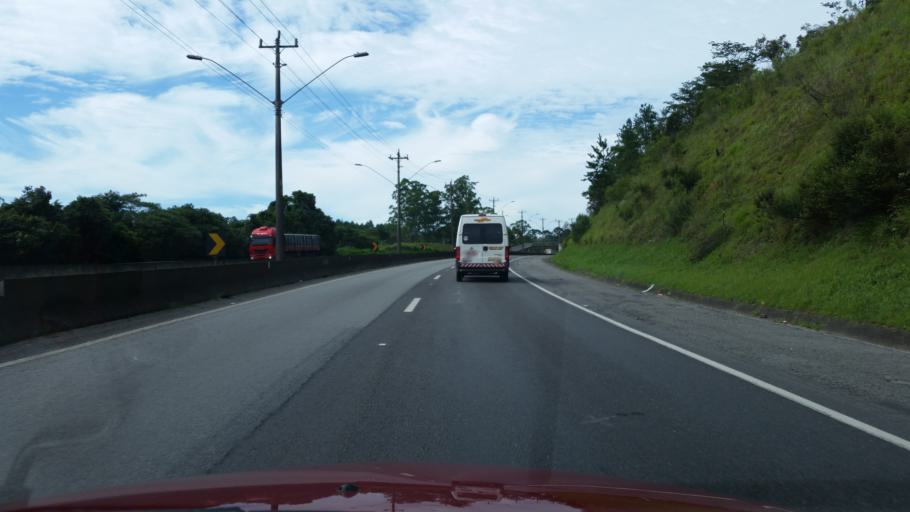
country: BR
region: Sao Paulo
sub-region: Itapecerica Da Serra
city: Itapecerica da Serra
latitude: -23.7574
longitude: -46.9026
